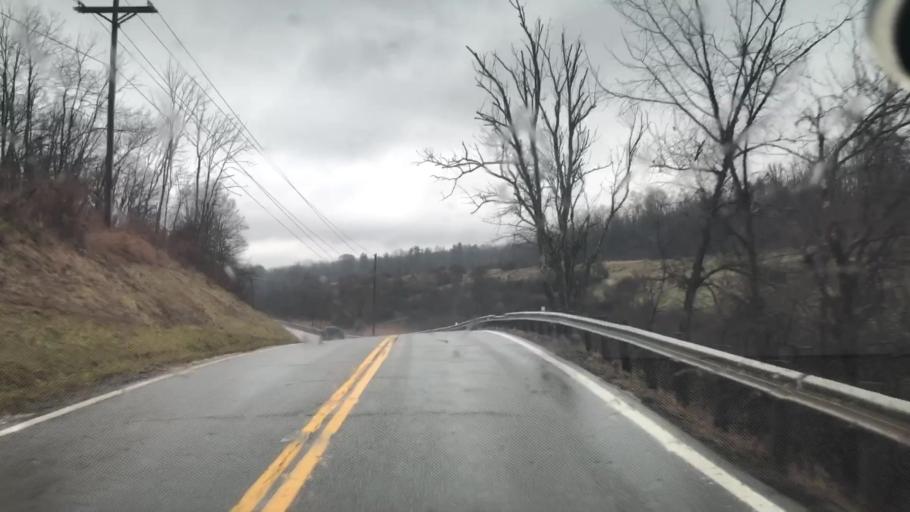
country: US
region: Ohio
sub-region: Harrison County
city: Cadiz
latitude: 40.1617
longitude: -80.9797
